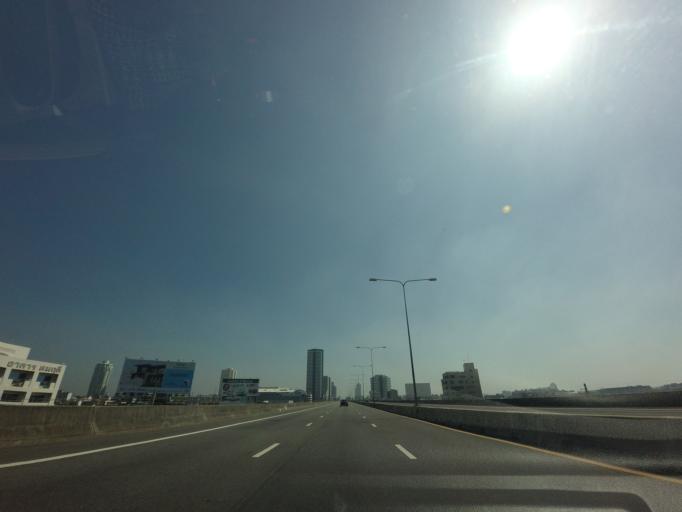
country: TH
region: Bangkok
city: Bang Na
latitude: 13.6694
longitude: 100.6263
